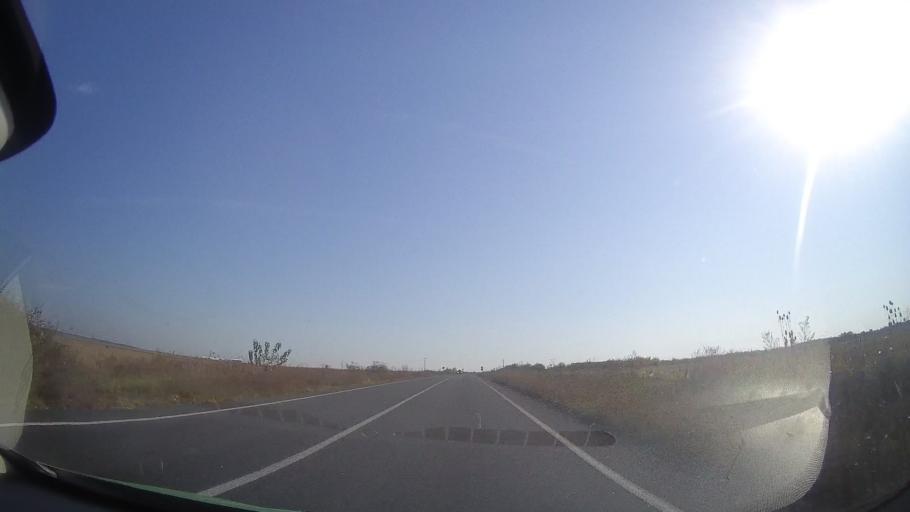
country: RO
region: Timis
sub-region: Comuna Topolovatu Mare
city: Topolovatu Mare
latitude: 45.7747
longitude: 21.6353
